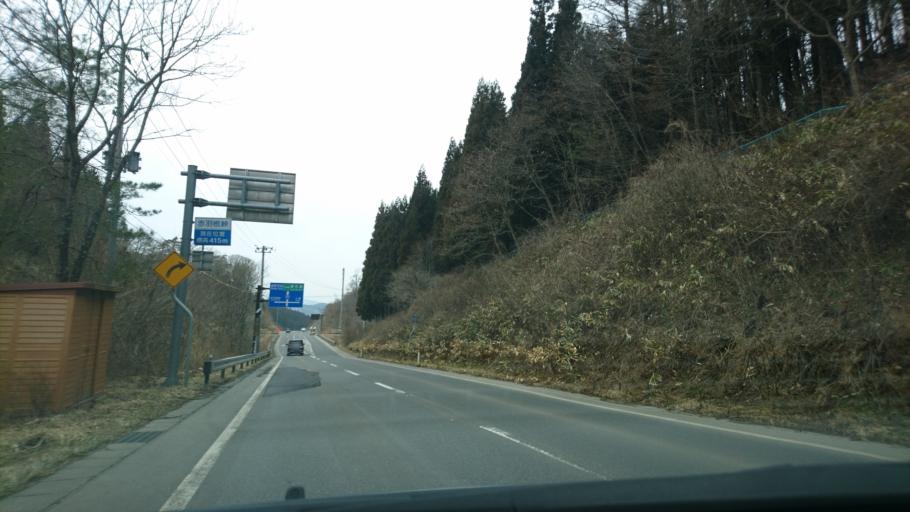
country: JP
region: Iwate
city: Tono
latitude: 39.2591
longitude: 141.5936
